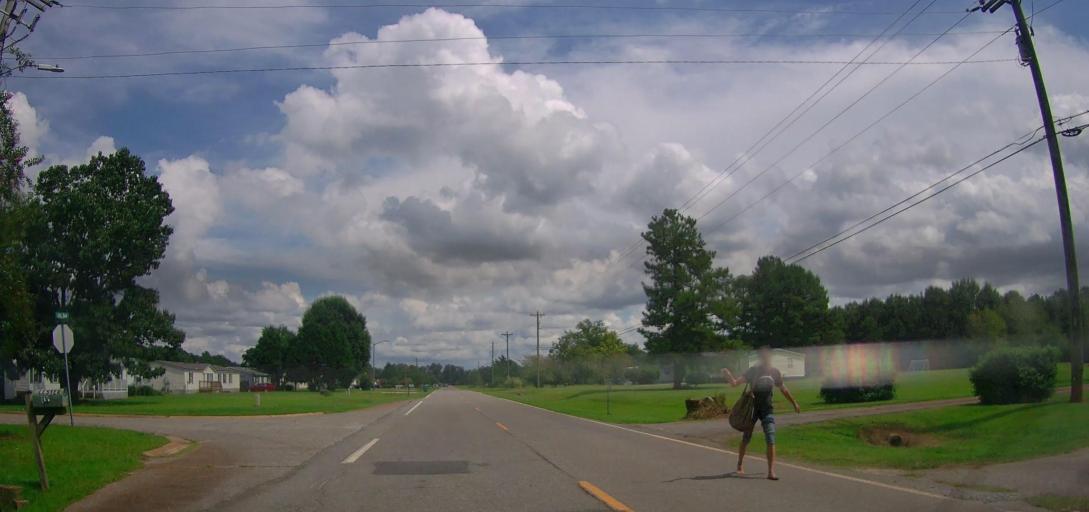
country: US
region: Georgia
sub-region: Houston County
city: Perry
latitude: 32.5108
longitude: -83.7355
